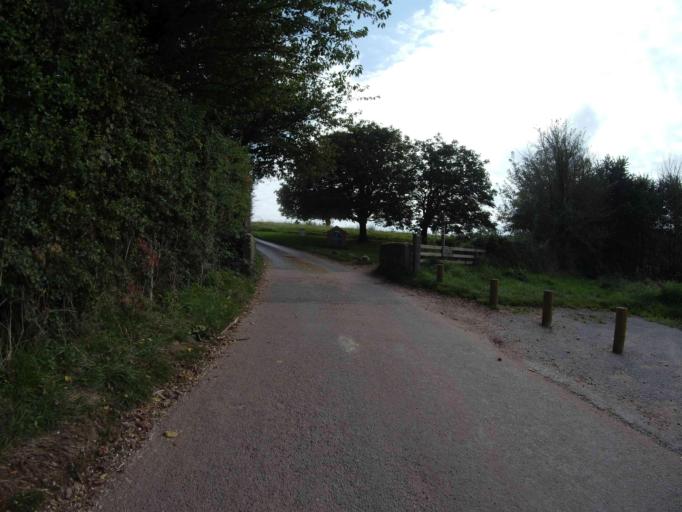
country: GB
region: England
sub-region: Devon
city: Budleigh Salterton
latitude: 50.6397
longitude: -3.3077
